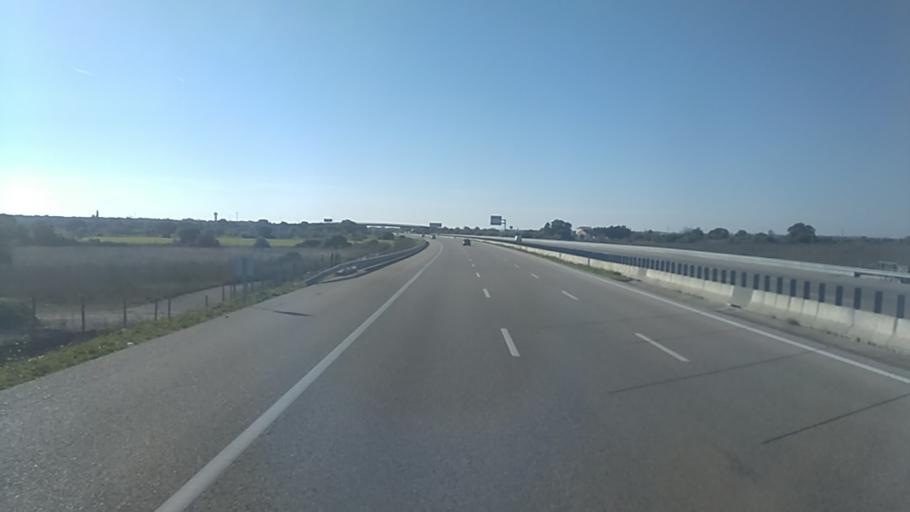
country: PT
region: Santarem
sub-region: Alcanena
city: Alcanena
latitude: 39.4143
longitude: -8.6347
